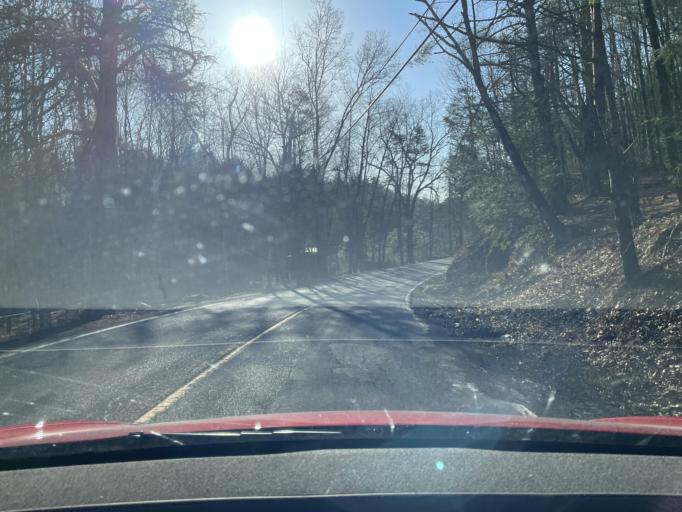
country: US
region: New York
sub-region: Ulster County
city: Saugerties South
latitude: 42.0437
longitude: -74.0058
